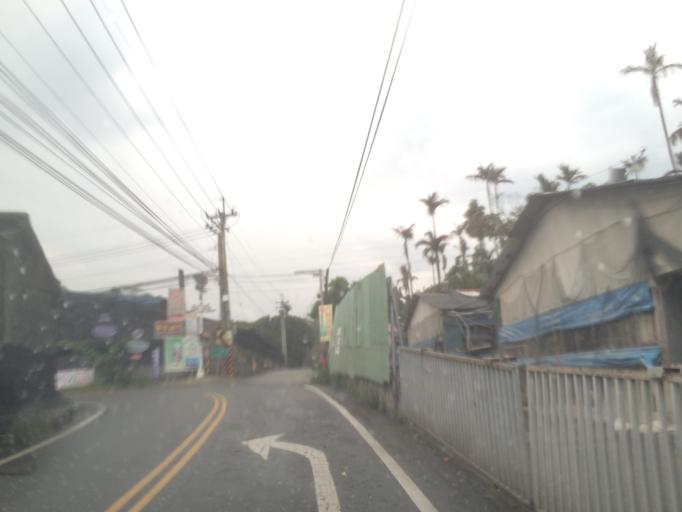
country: TW
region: Taiwan
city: Fengyuan
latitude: 24.1776
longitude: 120.8207
